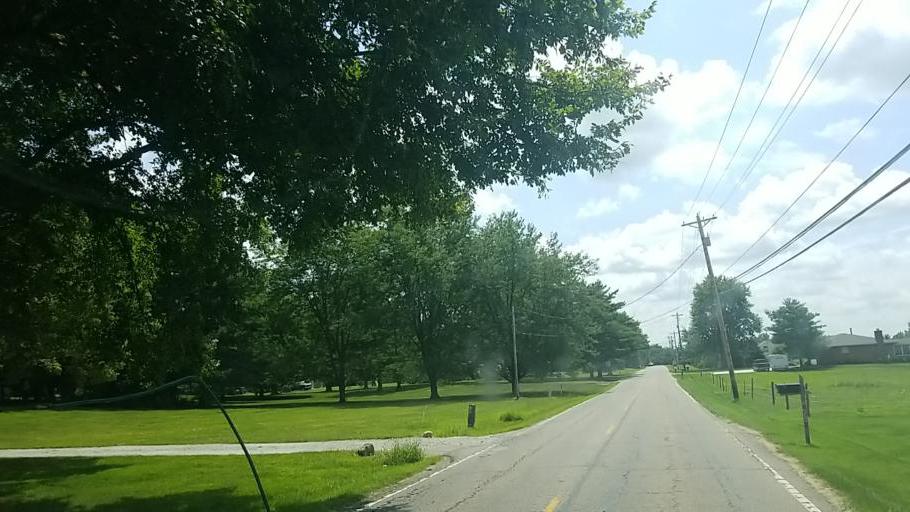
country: US
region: Ohio
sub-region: Fairfield County
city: Pickerington
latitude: 39.8952
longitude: -82.7485
